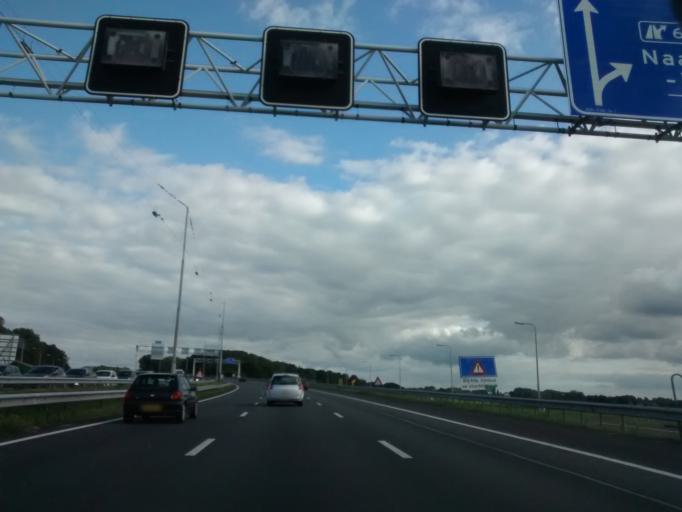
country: NL
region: North Holland
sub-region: Gemeente Naarden
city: Naarden
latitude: 52.3070
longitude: 5.1284
